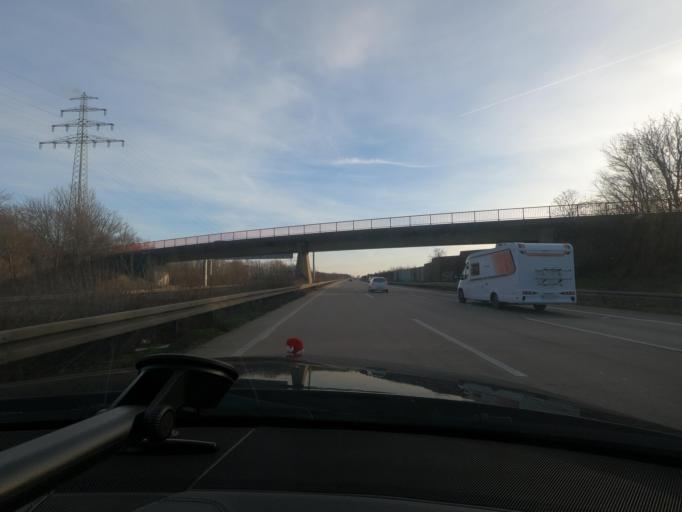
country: DE
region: Lower Saxony
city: Sarstedt
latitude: 52.2900
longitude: 9.8978
